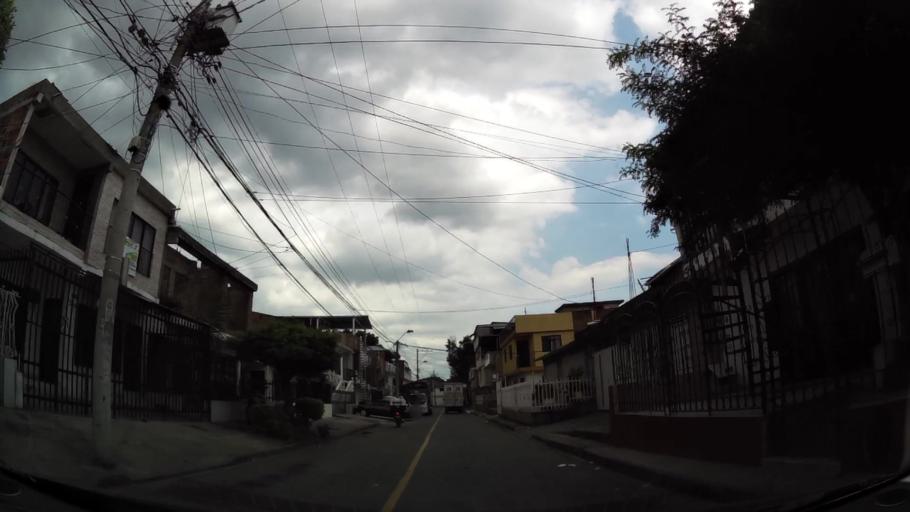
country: CO
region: Valle del Cauca
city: Cali
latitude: 3.4597
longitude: -76.4856
